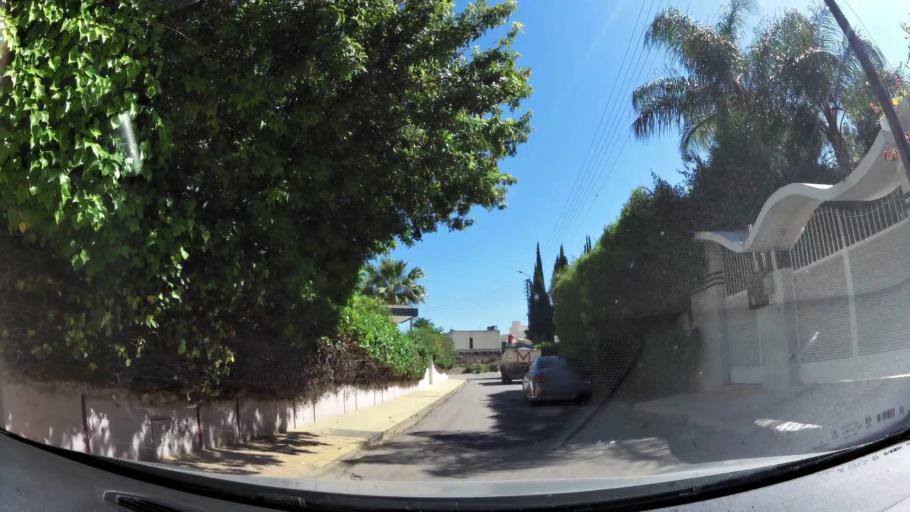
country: MA
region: Fes-Boulemane
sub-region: Fes
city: Fes
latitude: 34.0178
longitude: -4.9954
